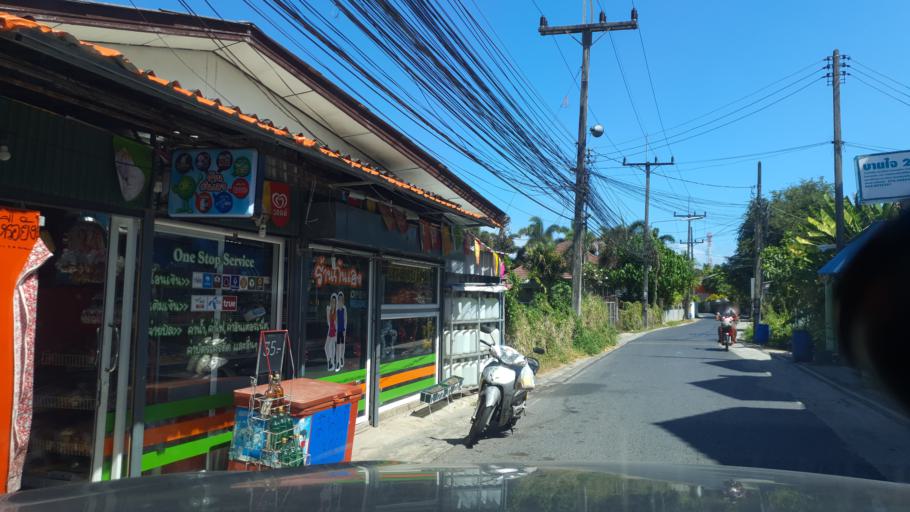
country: TH
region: Phuket
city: Ban Ko Kaeo
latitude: 7.9618
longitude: 98.3770
